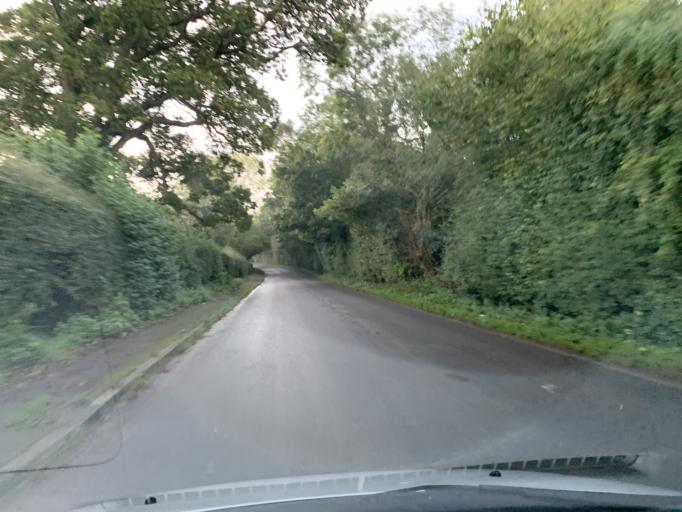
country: GB
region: England
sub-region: Wiltshire
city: Alderbury
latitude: 51.0504
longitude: -1.7495
